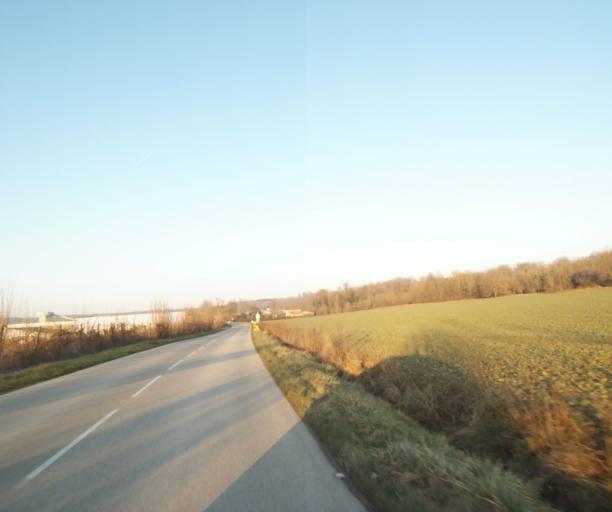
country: FR
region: Champagne-Ardenne
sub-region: Departement de la Haute-Marne
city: Bienville
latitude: 48.5952
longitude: 5.0420
